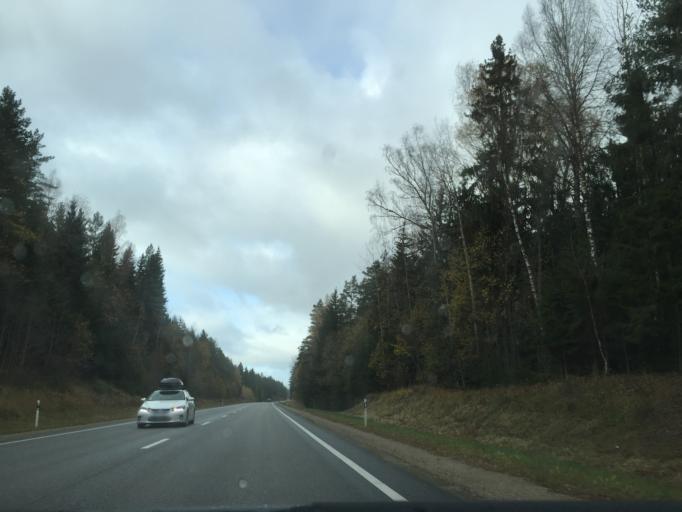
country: LV
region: Tukuma Rajons
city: Tukums
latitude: 57.0000
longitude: 23.0069
